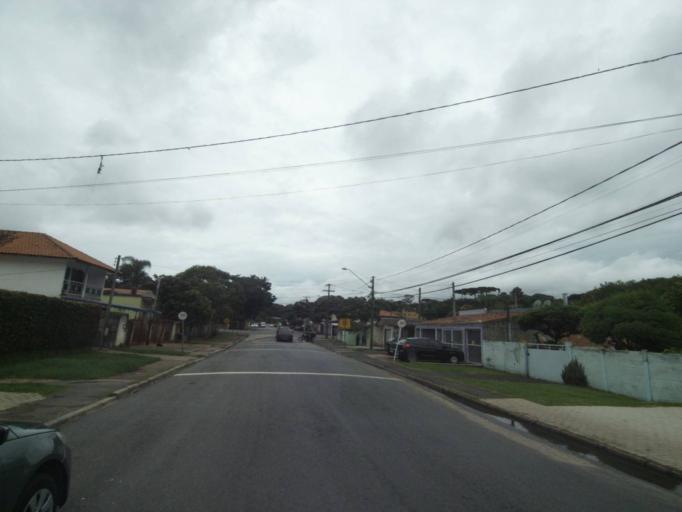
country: BR
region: Parana
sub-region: Curitiba
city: Curitiba
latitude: -25.4564
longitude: -49.3227
